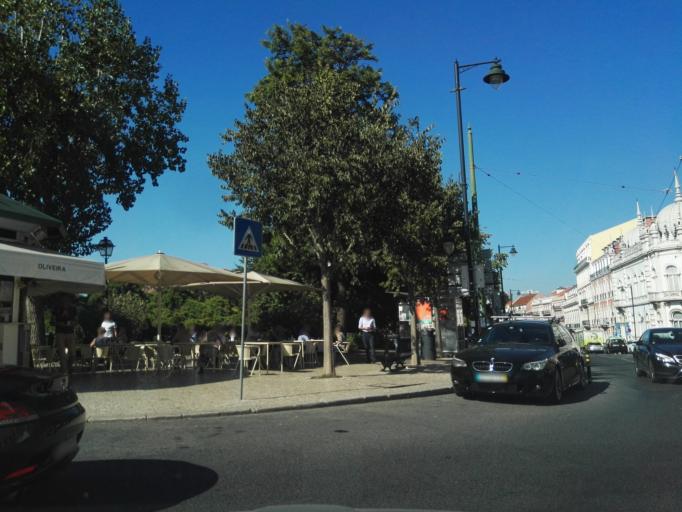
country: PT
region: Lisbon
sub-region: Lisbon
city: Lisbon
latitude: 38.7163
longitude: -9.1477
